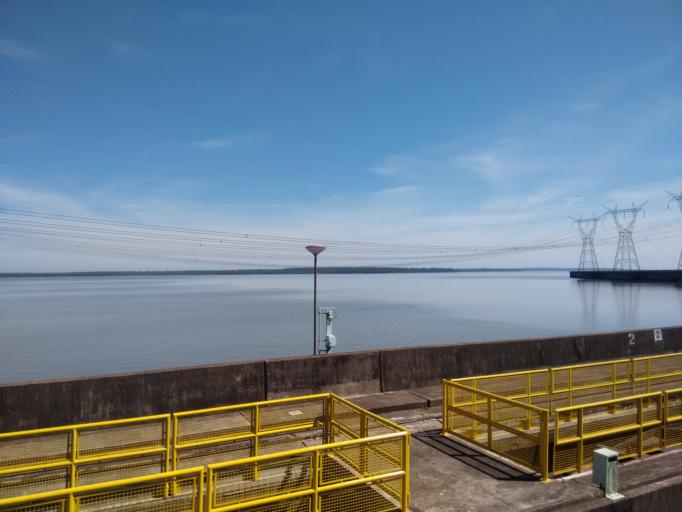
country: PY
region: Alto Parana
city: Ciudad del Este
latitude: -25.4144
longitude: -54.5991
